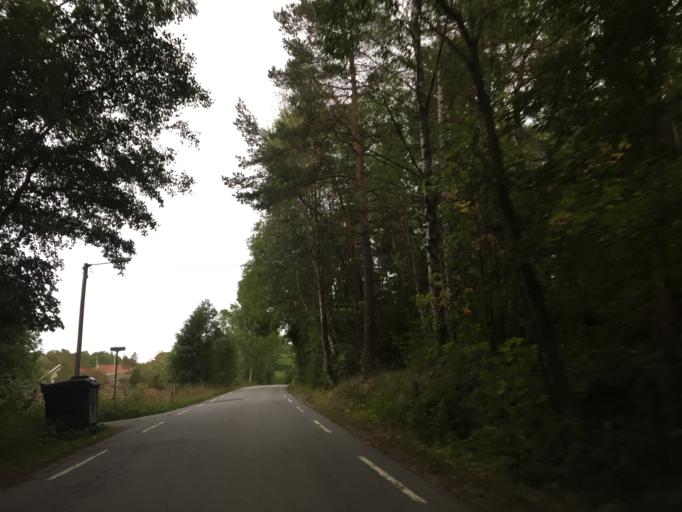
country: NO
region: Ostfold
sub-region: Hvaler
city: Skjaerhalden
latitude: 59.0745
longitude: 11.0050
